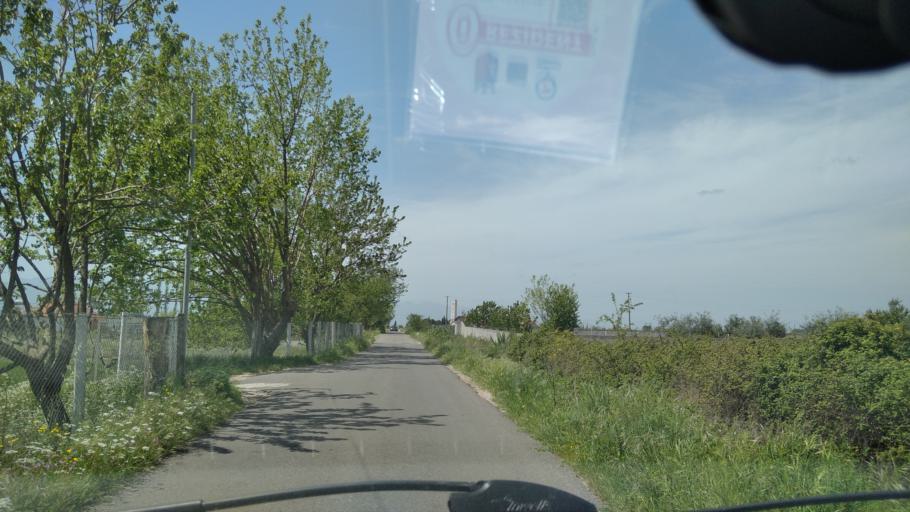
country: AL
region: Shkoder
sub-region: Rrethi i Malesia e Madhe
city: Gruemire
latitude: 42.1424
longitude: 19.5093
